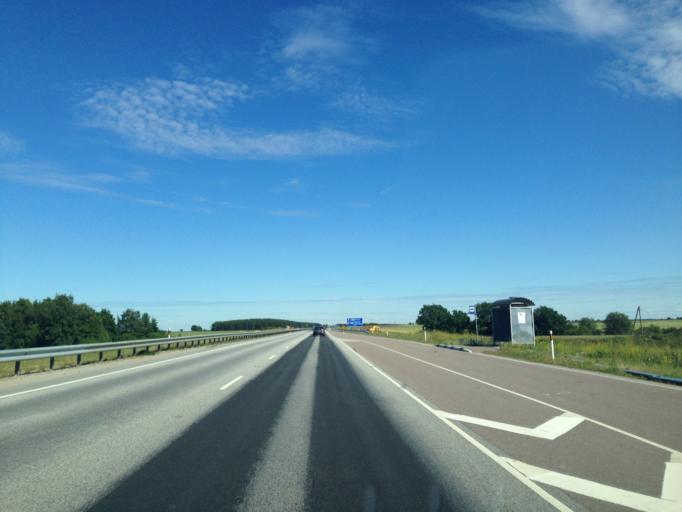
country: EE
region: Harju
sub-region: Maardu linn
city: Maardu
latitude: 59.4511
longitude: 25.0496
